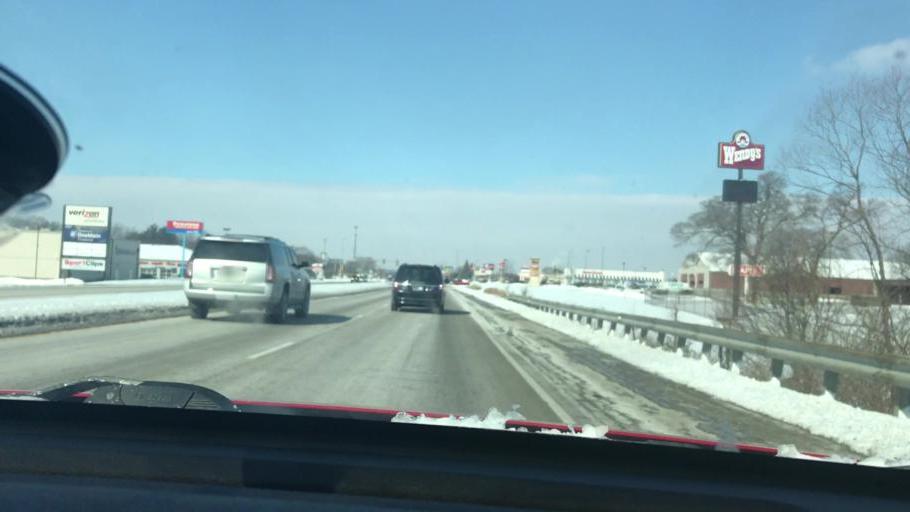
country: US
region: Illinois
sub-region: Tazewell County
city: Pekin
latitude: 40.5421
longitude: -89.5960
